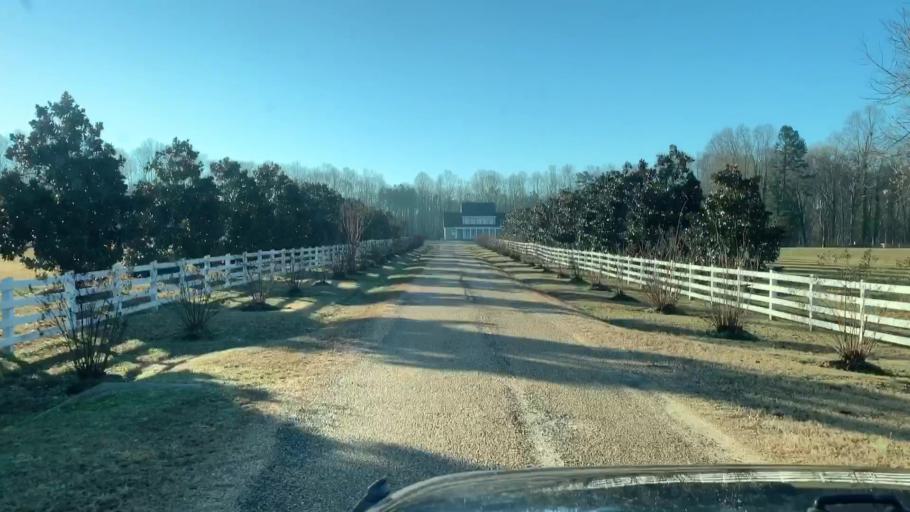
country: US
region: Virginia
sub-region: James City County
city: Williamsburg
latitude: 37.3841
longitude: -76.8207
